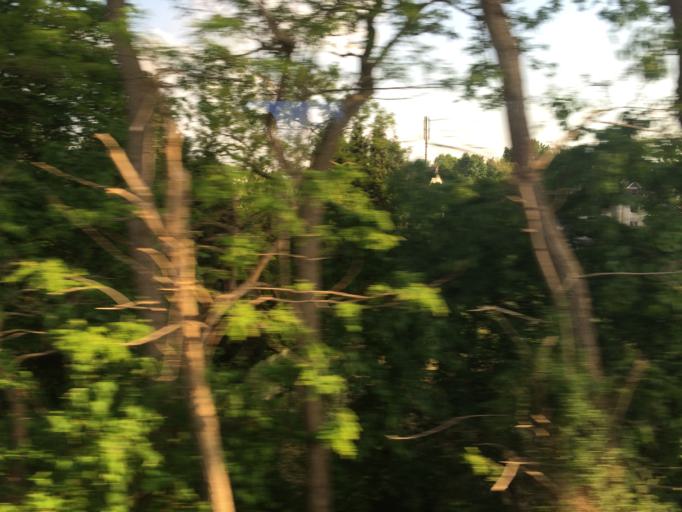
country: DE
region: North Rhine-Westphalia
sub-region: Regierungsbezirk Dusseldorf
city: Muelheim (Ruhr)
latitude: 51.4503
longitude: 6.8444
